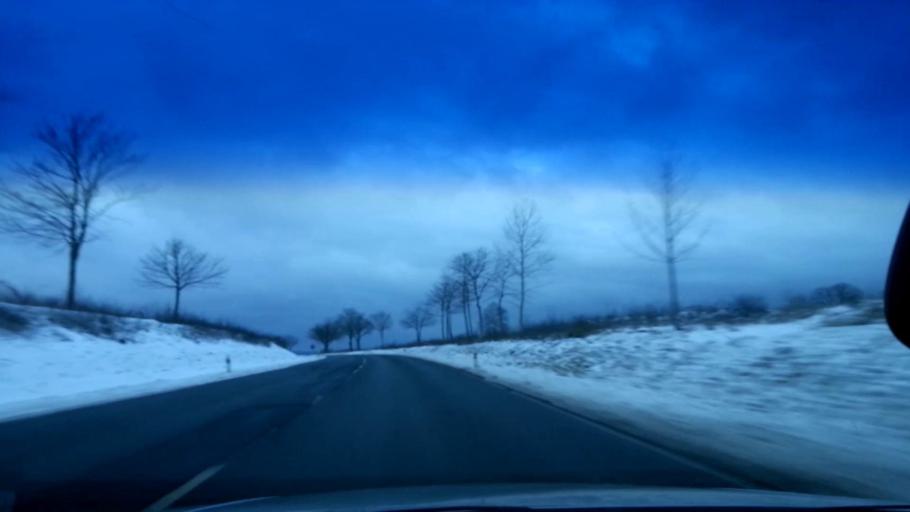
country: DE
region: Bavaria
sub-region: Upper Franconia
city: Marktleuthen
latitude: 50.1592
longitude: 12.0453
